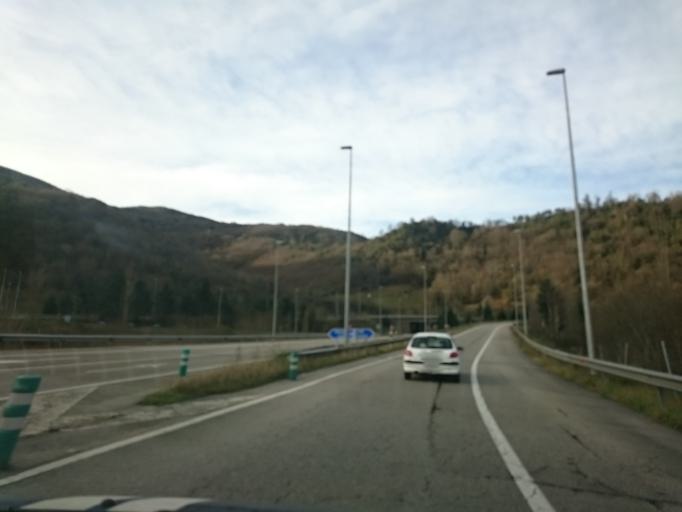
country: ES
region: Asturias
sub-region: Province of Asturias
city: Castandiello
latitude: 43.3014
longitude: -5.8380
